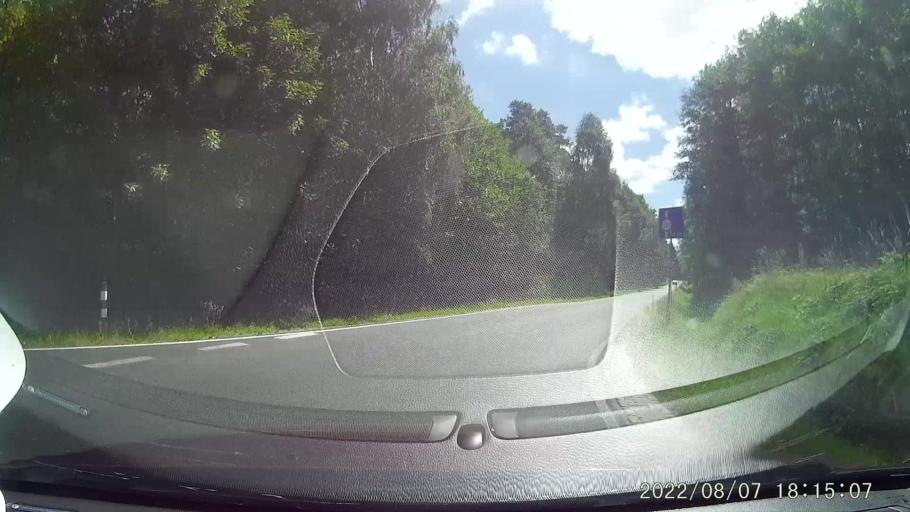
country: PL
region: Lower Silesian Voivodeship
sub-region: Powiat lubanski
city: Swieradow-Zdroj
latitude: 50.9078
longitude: 15.3309
